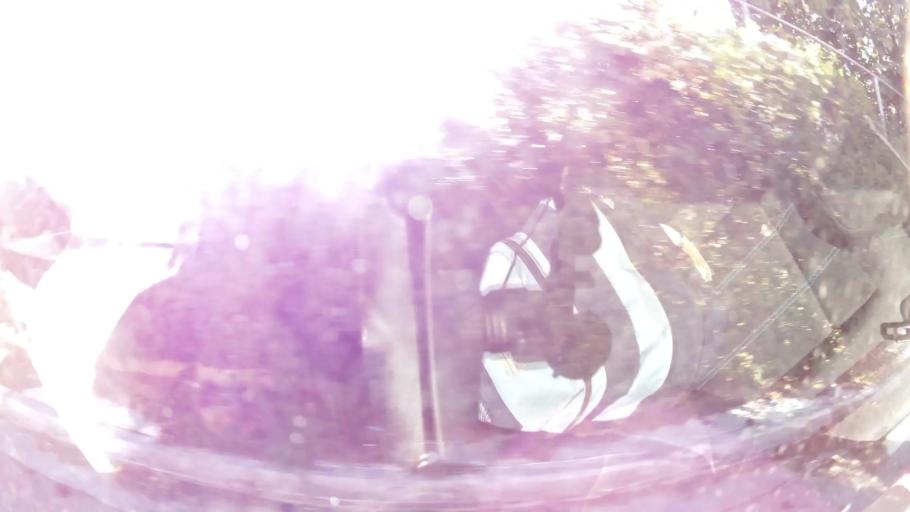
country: GR
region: Attica
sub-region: Nomarchia Anatolikis Attikis
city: Leondarion
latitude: 37.9929
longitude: 23.8590
